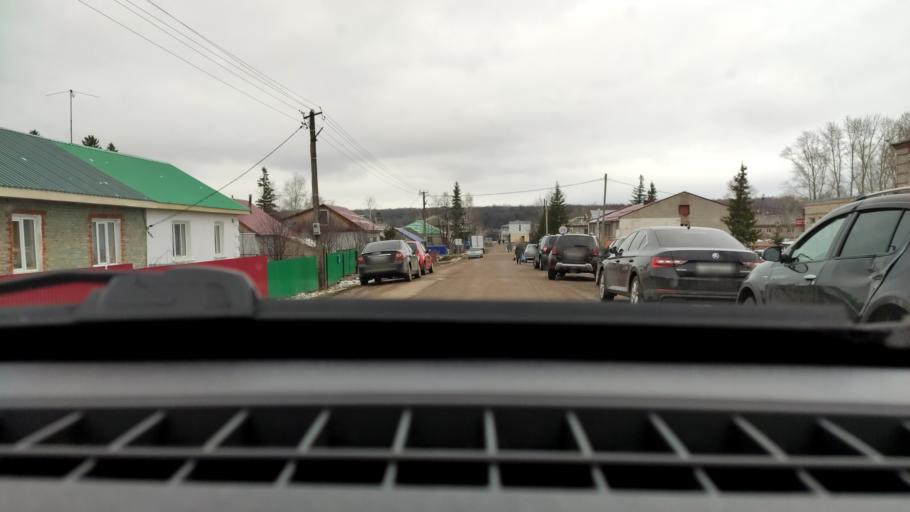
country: RU
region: Bashkortostan
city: Mikhaylovka
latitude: 54.8088
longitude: 55.8069
